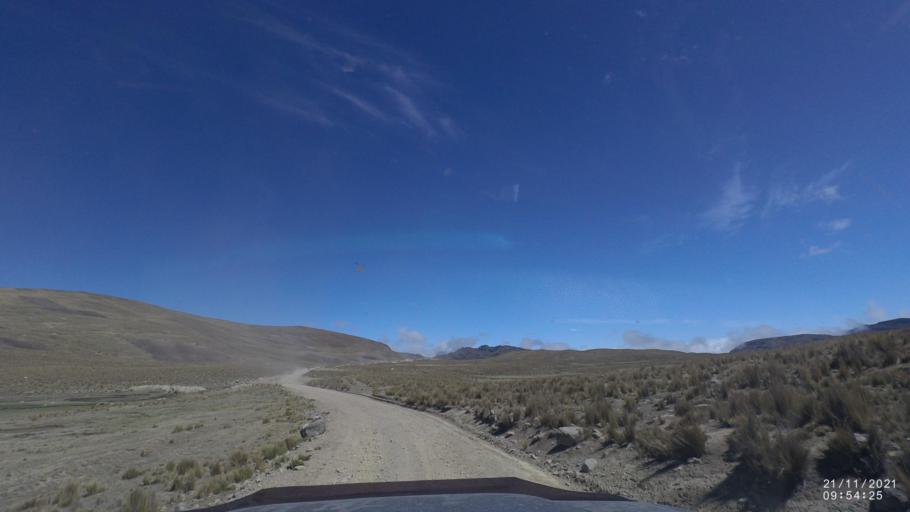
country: BO
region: Cochabamba
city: Cochabamba
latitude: -17.0534
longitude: -66.2608
